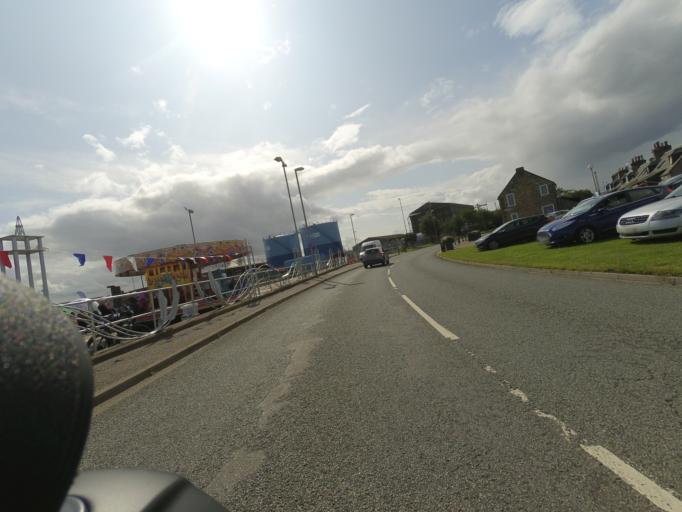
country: GB
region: Scotland
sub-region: Highland
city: Invergordon
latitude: 57.6865
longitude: -4.1679
